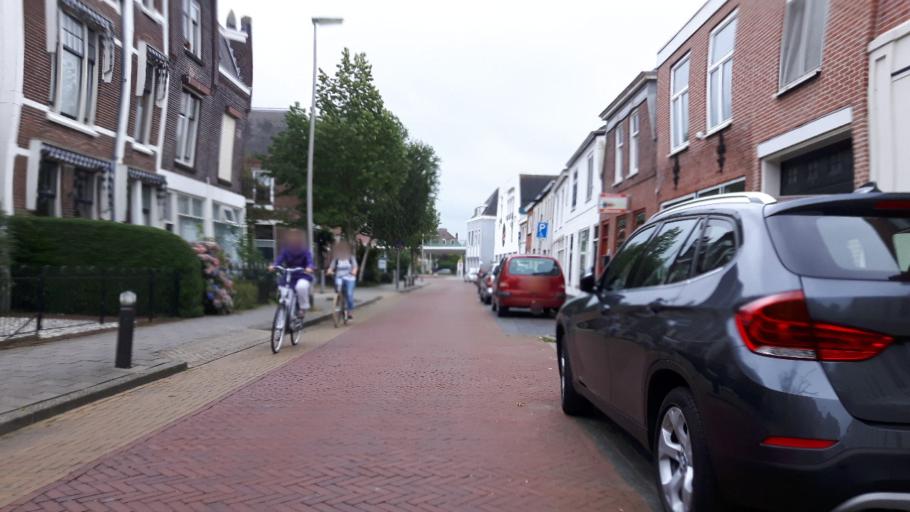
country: NL
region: South Holland
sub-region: Gemeente Alphen aan den Rijn
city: Alphen aan den Rijn
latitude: 52.1360
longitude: 4.6637
